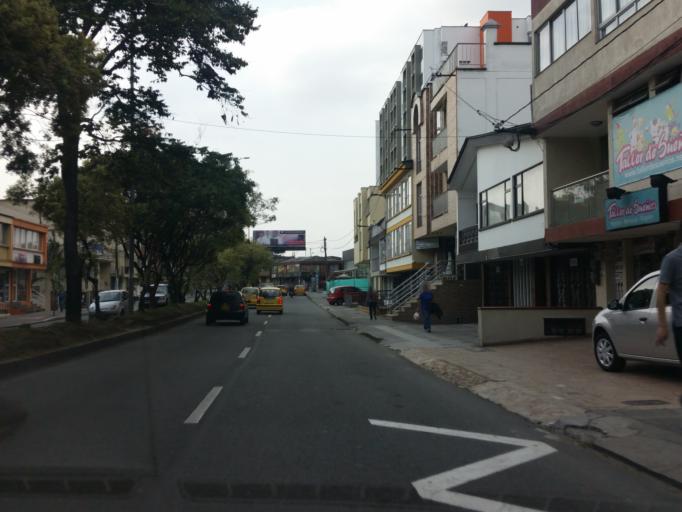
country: CO
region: Caldas
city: Manizales
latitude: 5.0631
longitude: -75.4954
